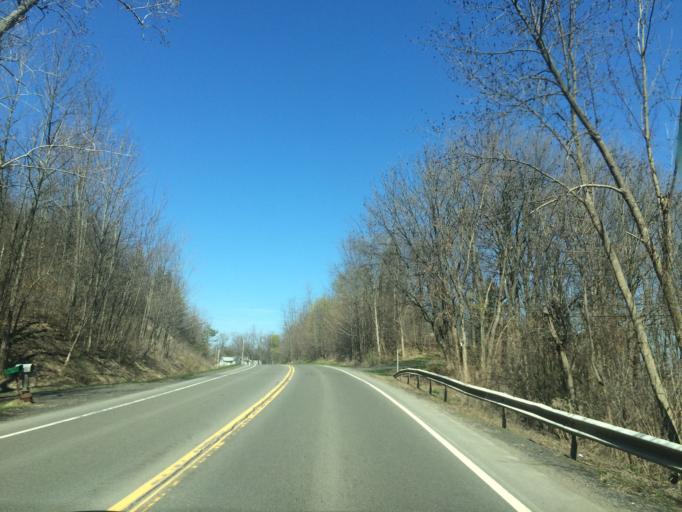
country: US
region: New York
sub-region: Wayne County
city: Macedon
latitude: 43.0951
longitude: -77.3603
